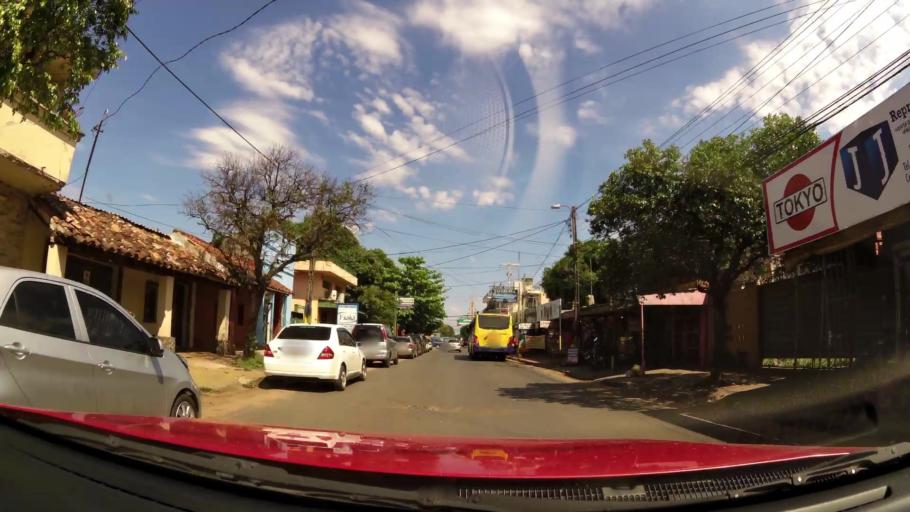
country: PY
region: Central
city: San Lorenzo
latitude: -25.2692
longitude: -57.4907
